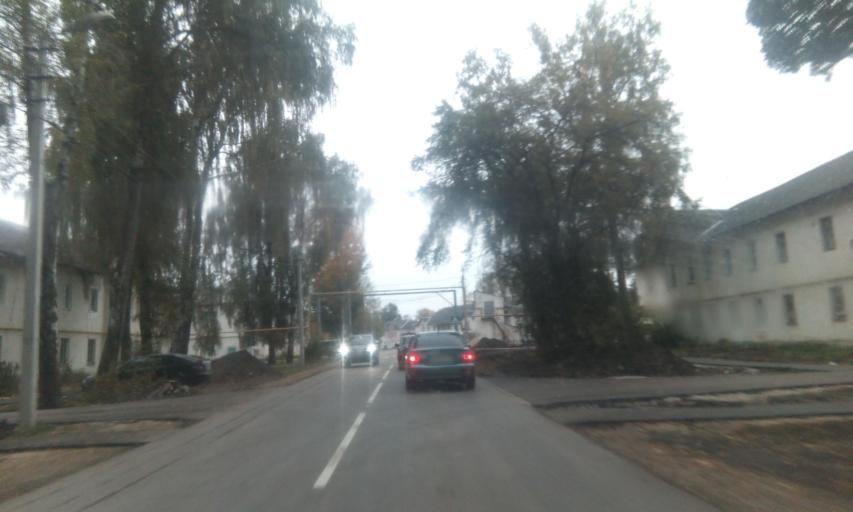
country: RU
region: Tula
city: Partizan
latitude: 53.9506
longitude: 38.0973
